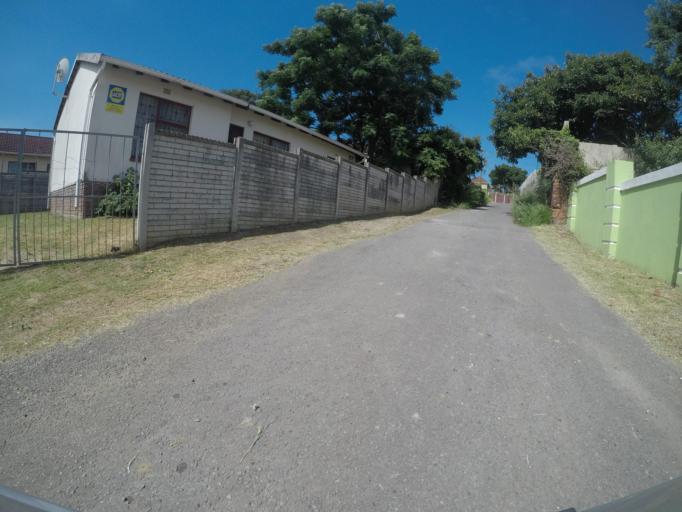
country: ZA
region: Eastern Cape
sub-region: Buffalo City Metropolitan Municipality
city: East London
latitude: -32.9762
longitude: 27.8906
